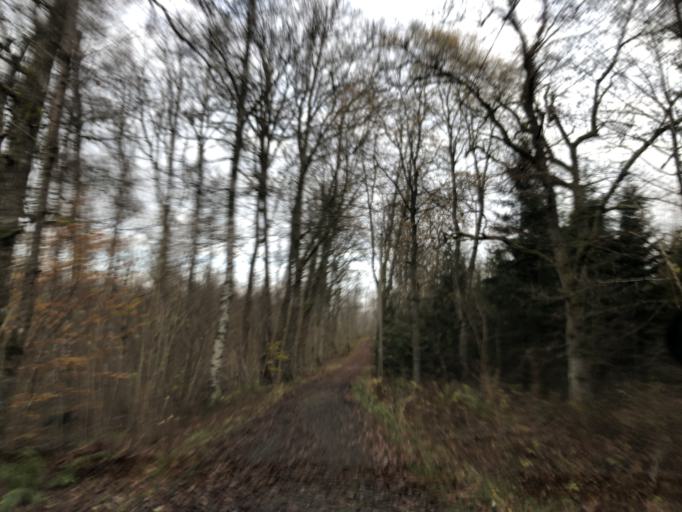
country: SE
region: Vaestra Goetaland
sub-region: Ulricehamns Kommun
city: Ulricehamn
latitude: 57.7226
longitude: 13.3081
